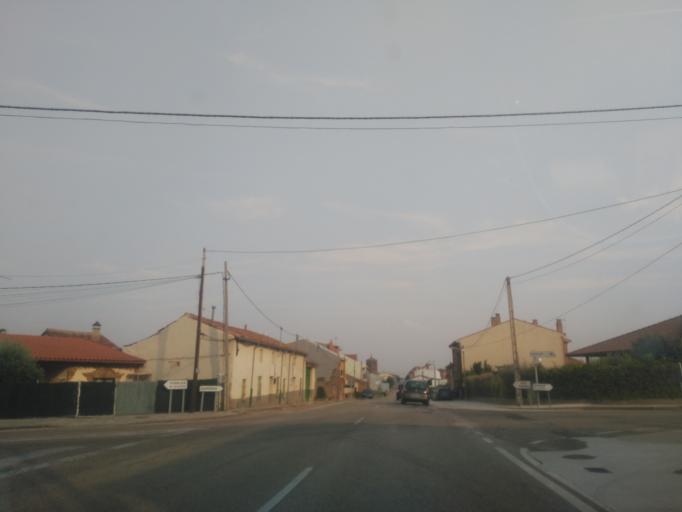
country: ES
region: Castille and Leon
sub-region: Provincia de Zamora
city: Tabara
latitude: 41.8294
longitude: -5.9629
